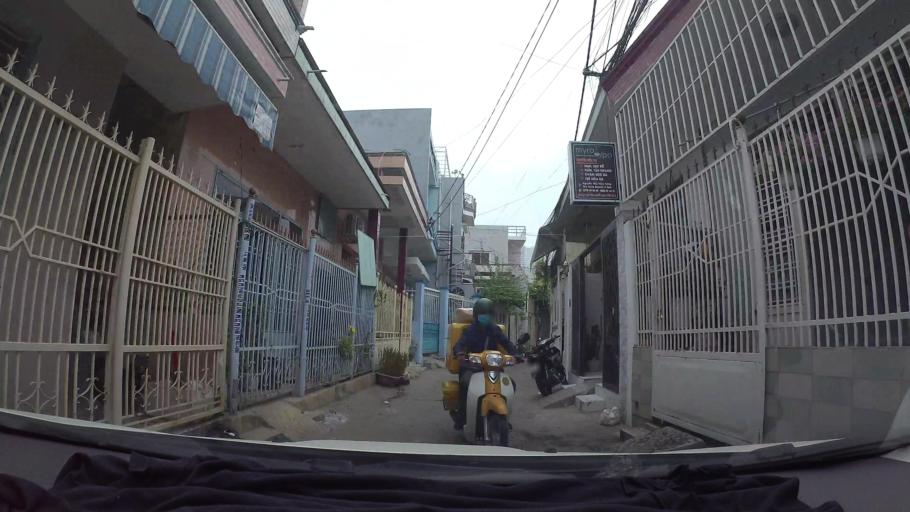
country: VN
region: Da Nang
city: Thanh Khe
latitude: 16.0675
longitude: 108.1990
